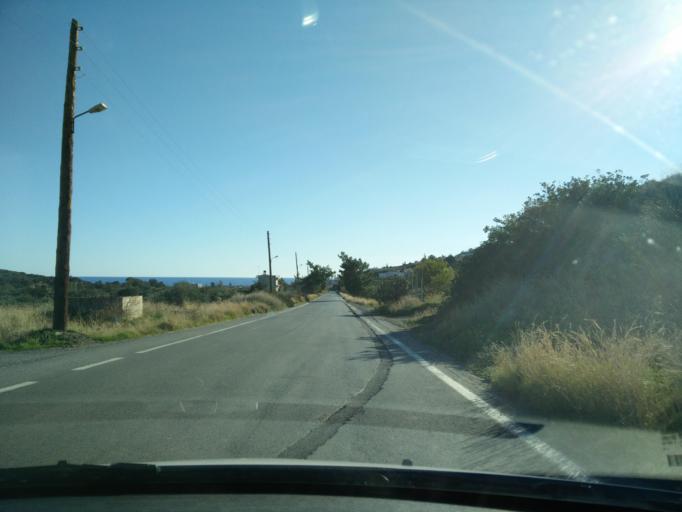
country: GR
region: Crete
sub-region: Nomos Lasithiou
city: Gra Liyia
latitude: 35.0145
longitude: 25.5834
